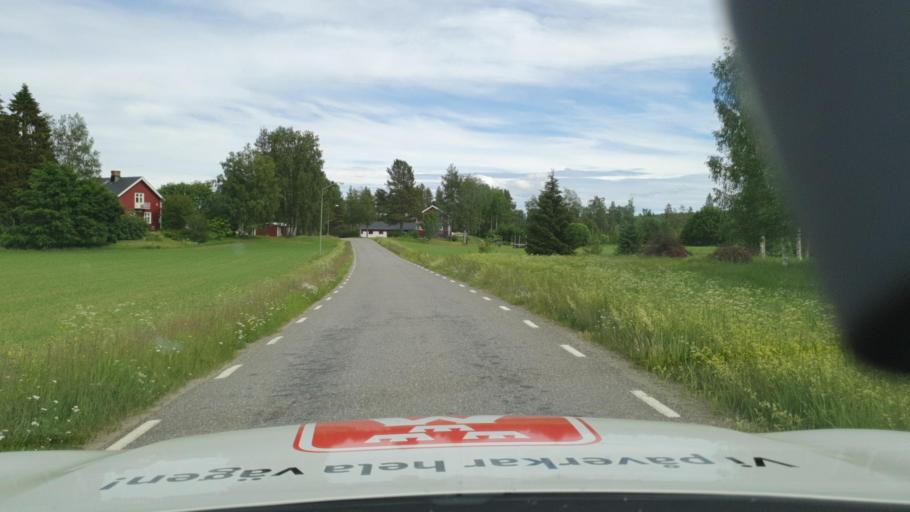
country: SE
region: Vaesterbotten
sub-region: Skelleftea Kommun
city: Burtraesk
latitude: 64.4972
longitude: 20.8614
